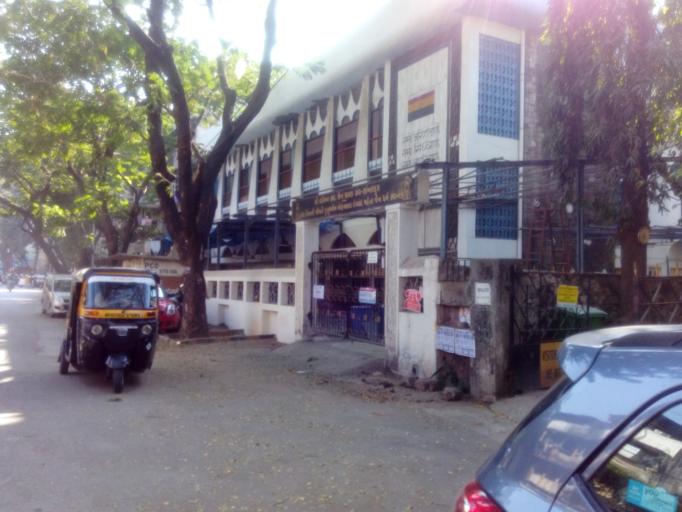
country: IN
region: Maharashtra
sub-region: Mumbai Suburban
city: Mumbai
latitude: 19.0845
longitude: 72.8407
